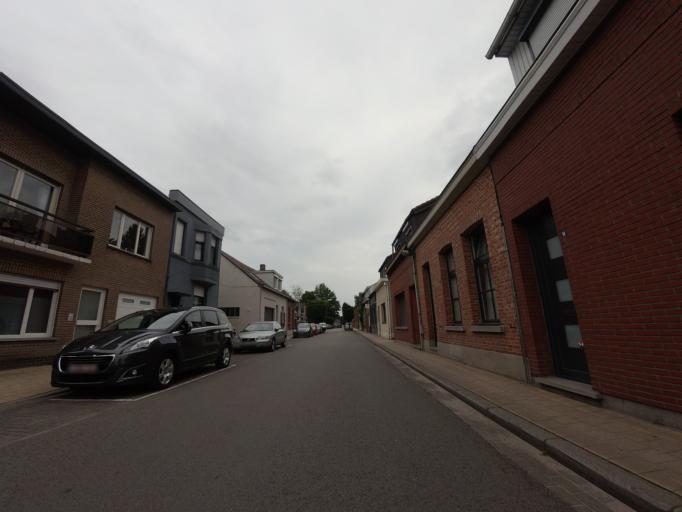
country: BE
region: Flanders
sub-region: Provincie Antwerpen
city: Schilde
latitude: 51.2394
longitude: 4.5831
